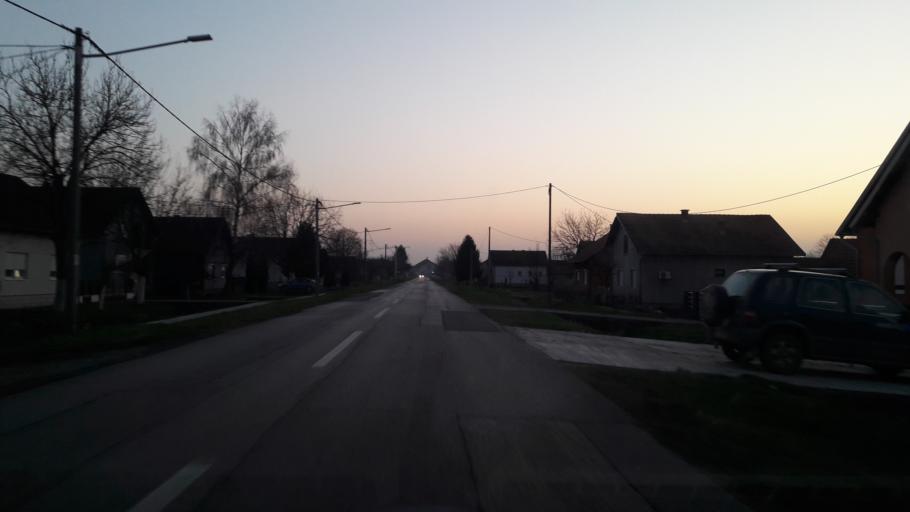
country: HR
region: Vukovarsko-Srijemska
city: Nijemci
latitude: 45.1866
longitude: 19.0150
